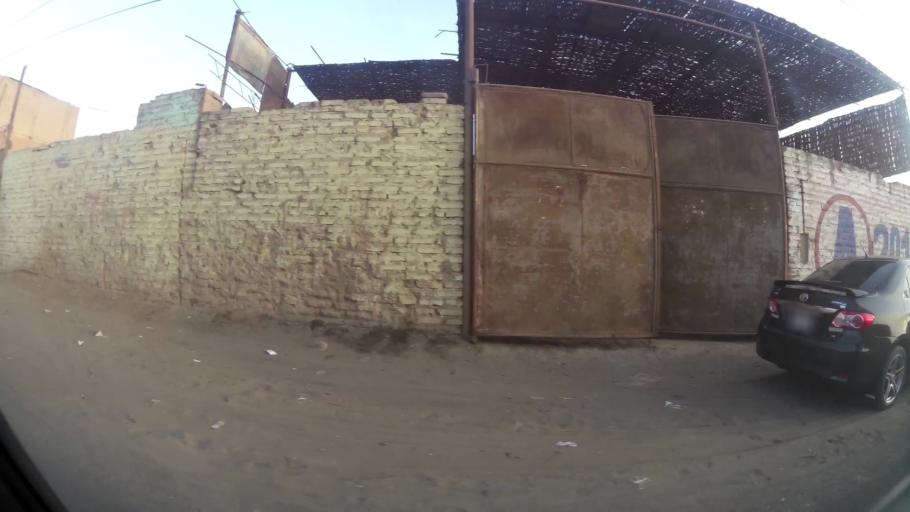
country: PE
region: Lima
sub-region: Huaura
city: Huacho
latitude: -11.1095
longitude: -77.5977
